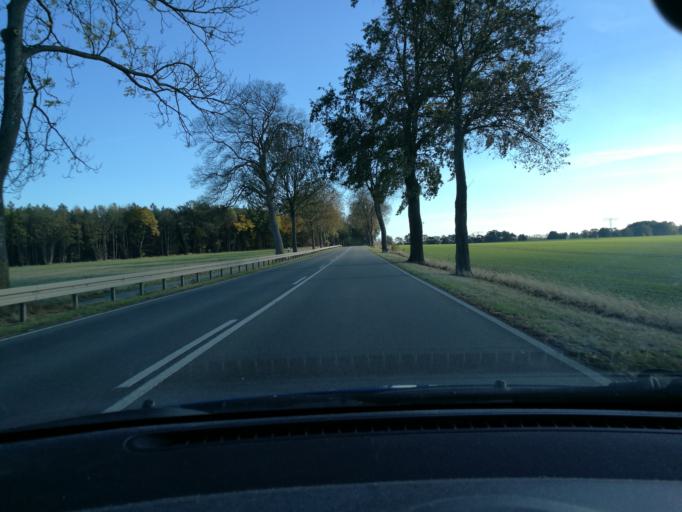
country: DE
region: Brandenburg
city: Perleberg
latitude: 53.1122
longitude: 11.8186
